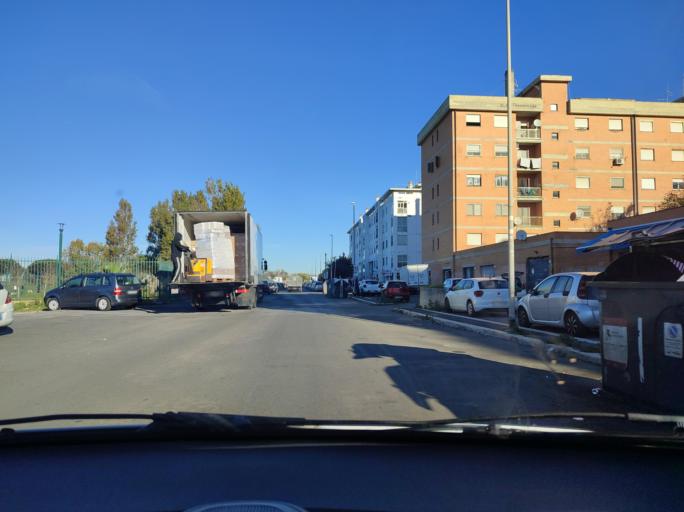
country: IT
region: Latium
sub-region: Citta metropolitana di Roma Capitale
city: Lido di Ostia
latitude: 41.7414
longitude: 12.2633
